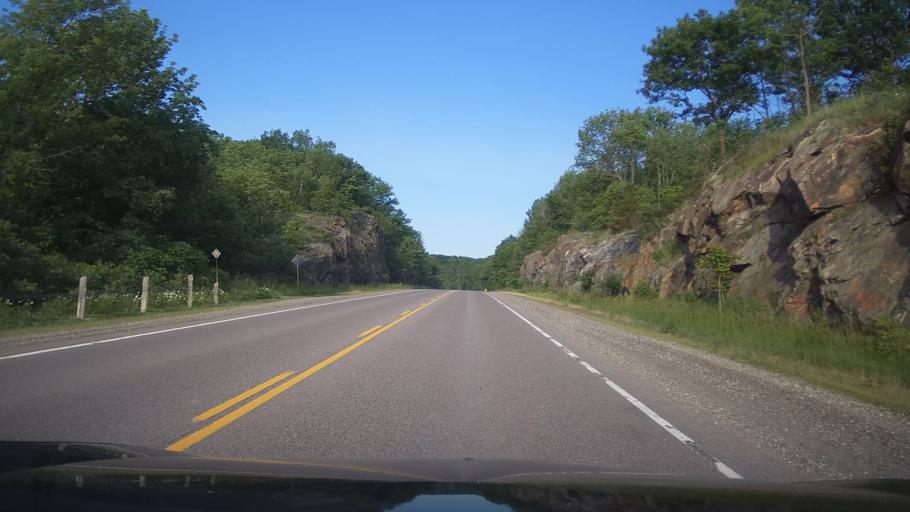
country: CA
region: Ontario
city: Perth
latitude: 44.7858
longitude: -76.7140
